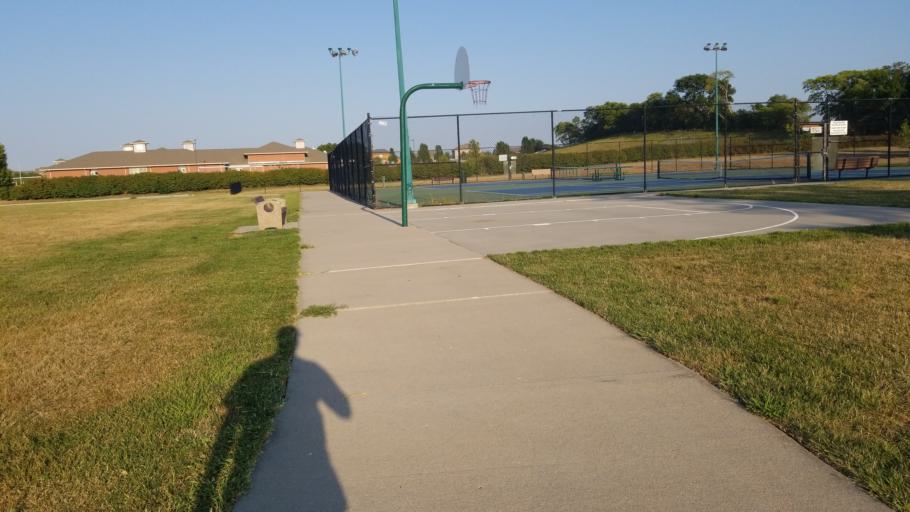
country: US
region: Nebraska
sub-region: Sarpy County
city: Papillion
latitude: 41.1264
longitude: -95.9943
